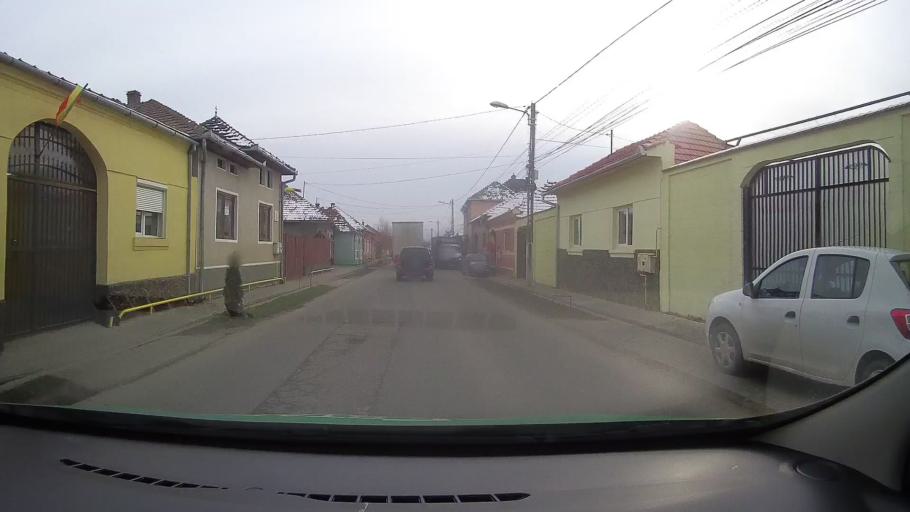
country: RO
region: Hunedoara
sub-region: Comuna Geoagiu
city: Geoagiu
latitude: 45.9042
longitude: 23.2230
